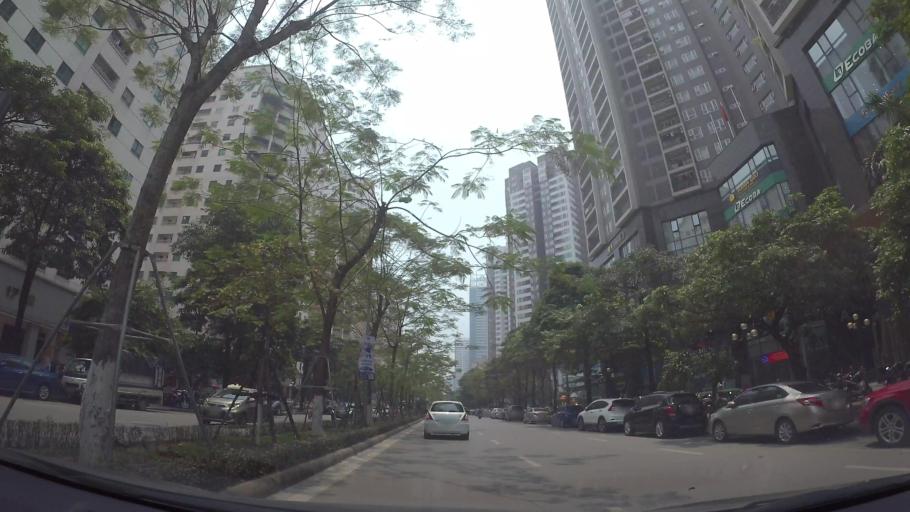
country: VN
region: Ha Noi
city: Thanh Xuan
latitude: 21.0091
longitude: 105.8008
